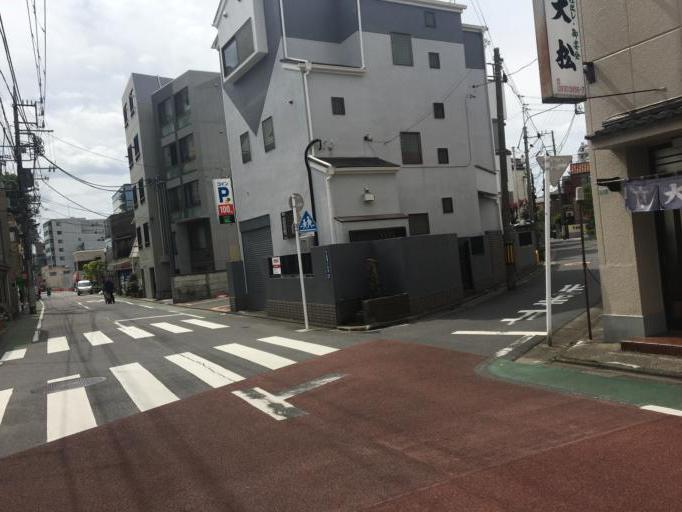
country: JP
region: Saitama
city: Shimotoda
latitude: 35.7645
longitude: 139.6701
